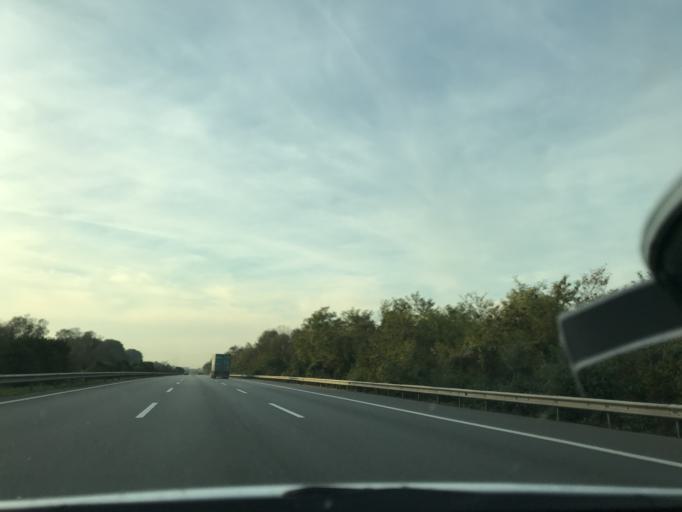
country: TR
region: Duzce
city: Cilimli
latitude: 40.8210
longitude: 31.0693
